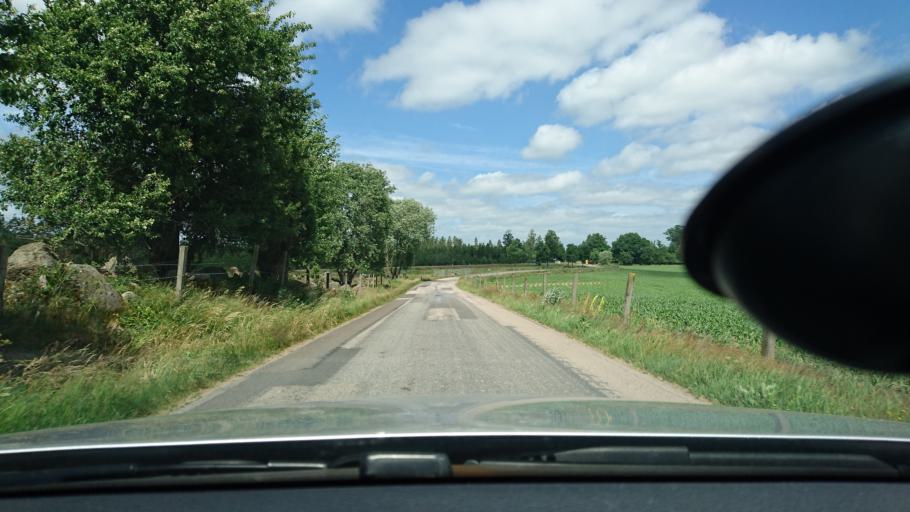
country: SE
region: Kronoberg
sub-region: Alvesta Kommun
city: Moheda
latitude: 56.9528
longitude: 14.5700
